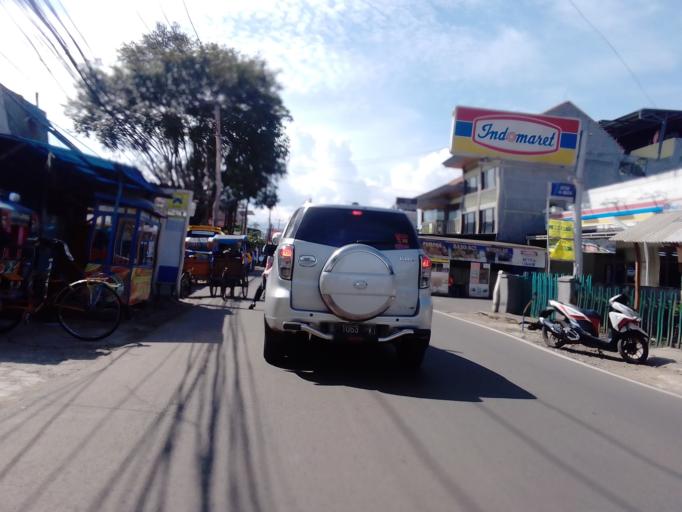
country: ID
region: West Java
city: Bandung
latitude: -6.9469
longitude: 107.6626
